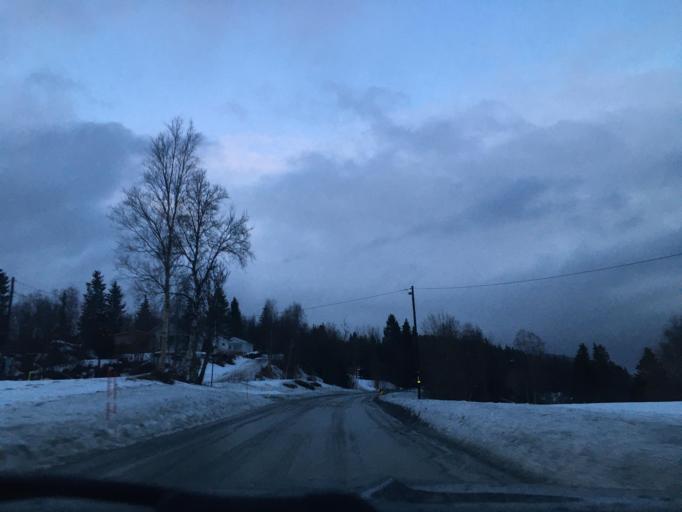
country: NO
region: Nordland
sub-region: Rana
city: Hauknes
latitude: 66.3033
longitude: 13.9379
